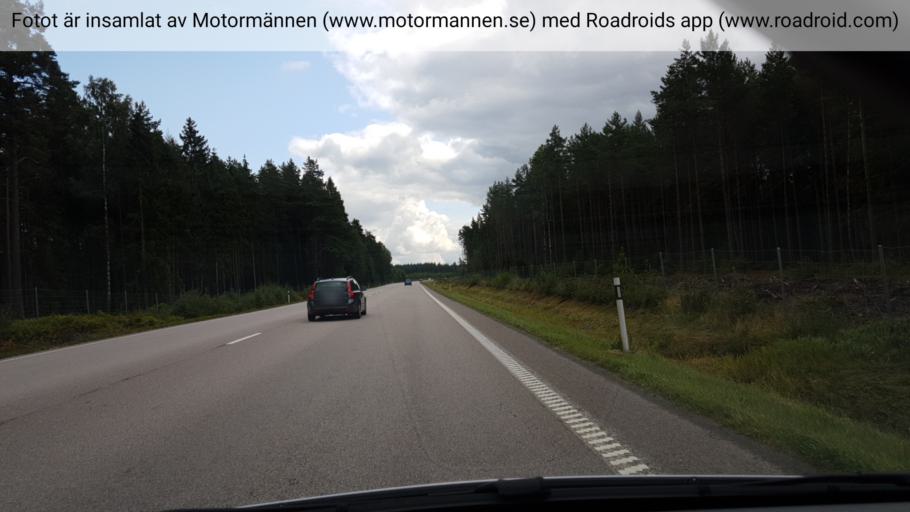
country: SE
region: Vaestra Goetaland
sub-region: Lidkopings Kommun
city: Lidkoping
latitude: 58.4840
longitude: 13.1948
